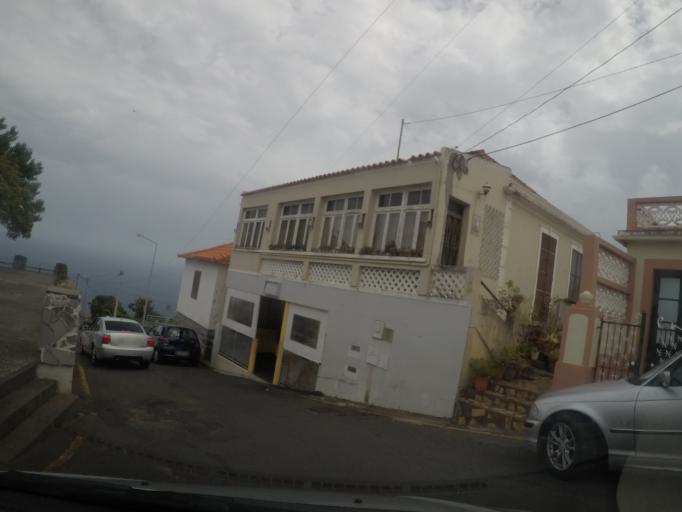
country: PT
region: Madeira
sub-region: Santa Cruz
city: Santa Cruz
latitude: 32.6746
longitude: -16.8114
